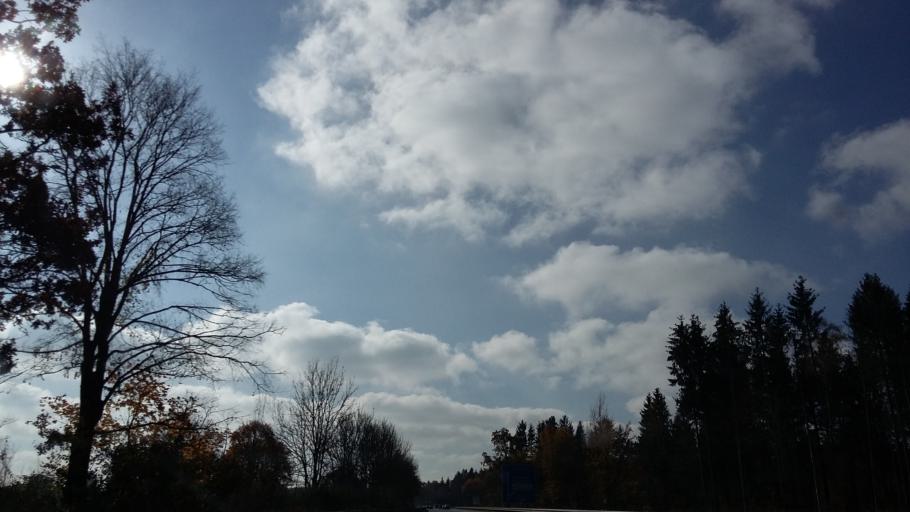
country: DE
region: Bavaria
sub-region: Upper Bavaria
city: Unterhaching
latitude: 48.0657
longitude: 11.5961
